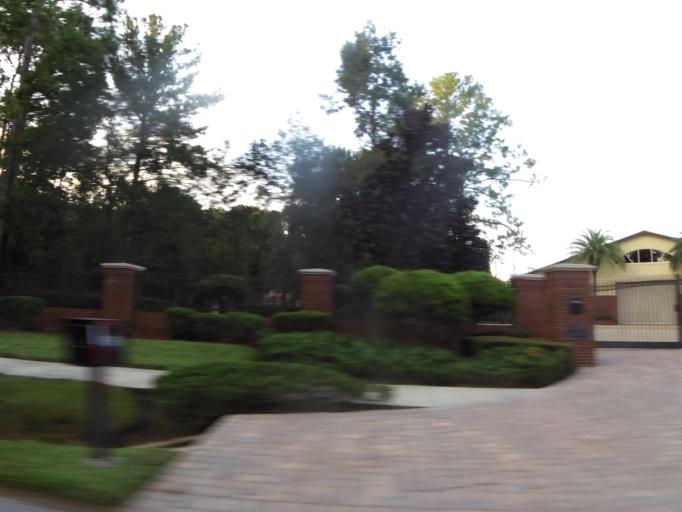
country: US
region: Florida
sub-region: Saint Johns County
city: Fruit Cove
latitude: 30.1796
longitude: -81.6312
